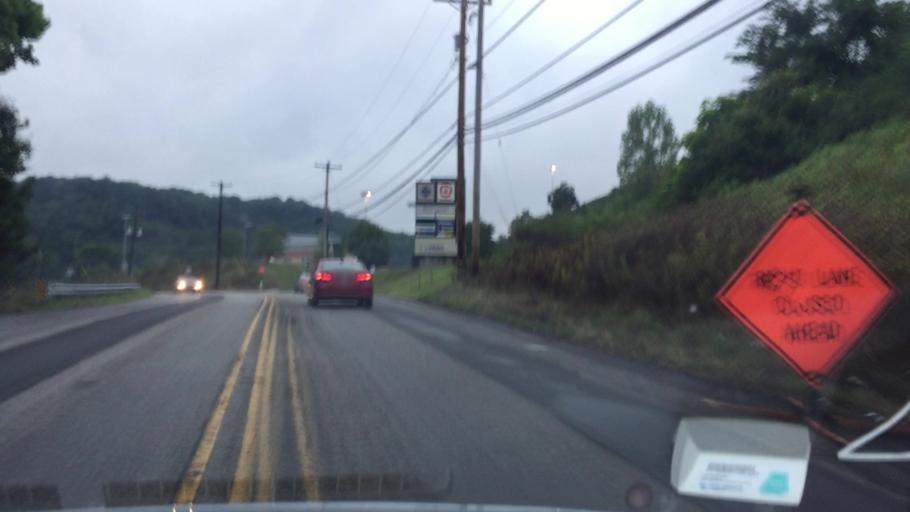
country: US
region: Pennsylvania
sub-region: Allegheny County
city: Ben Avon
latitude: 40.5319
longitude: -80.0666
